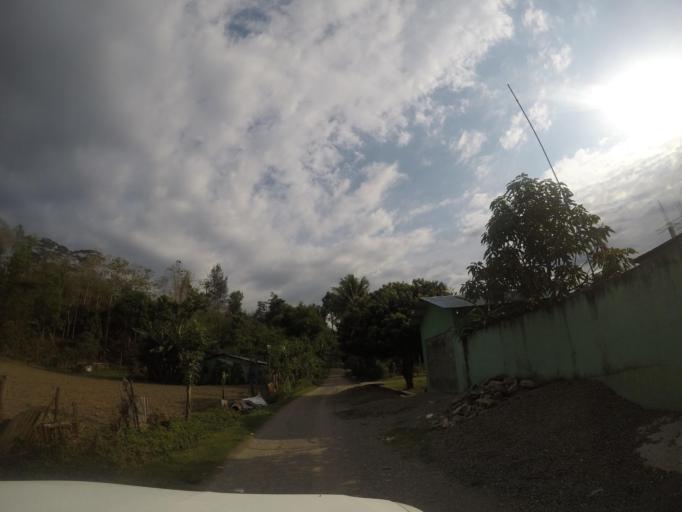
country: TL
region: Ermera
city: Gleno
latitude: -8.7206
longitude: 125.4373
